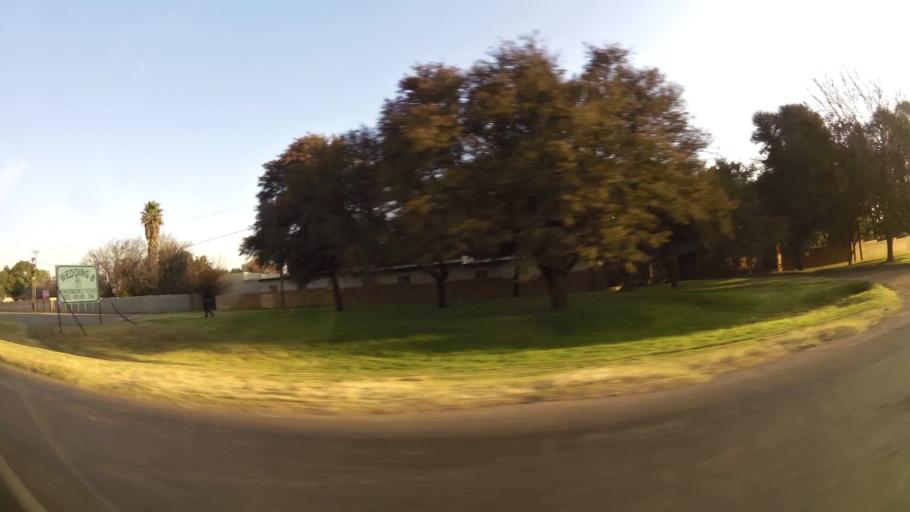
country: ZA
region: Gauteng
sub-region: West Rand District Municipality
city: Randfontein
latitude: -26.2027
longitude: 27.6855
